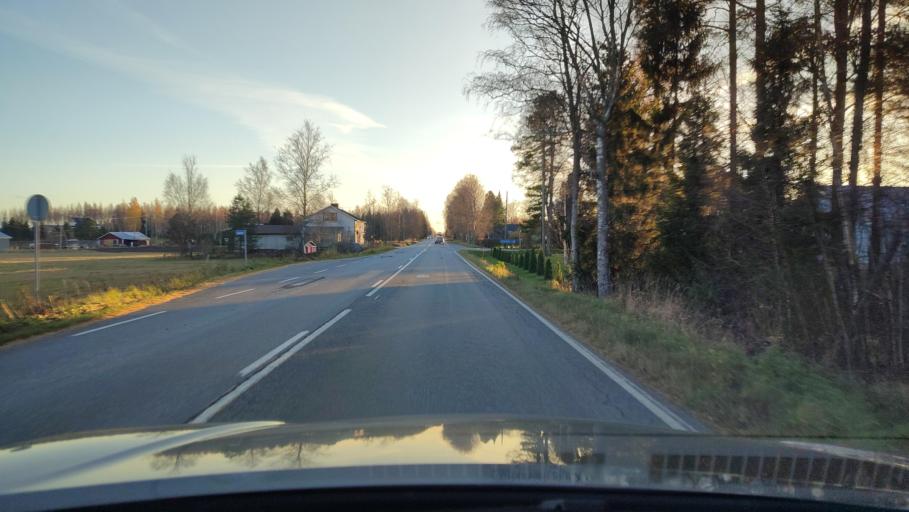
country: FI
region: Ostrobothnia
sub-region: Sydosterbotten
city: Naerpes
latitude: 62.5227
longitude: 21.3731
